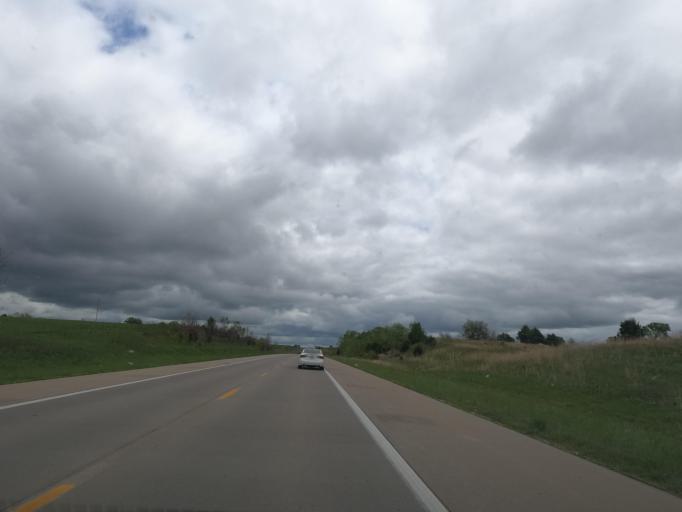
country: US
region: Kansas
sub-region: Montgomery County
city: Cherryvale
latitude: 37.3483
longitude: -95.5995
